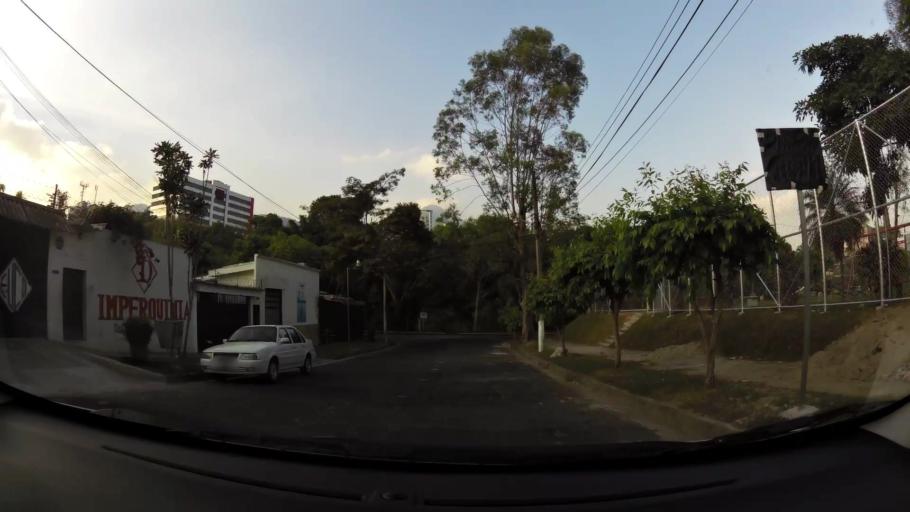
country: SV
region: La Libertad
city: Antiguo Cuscatlan
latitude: 13.7018
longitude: -89.2466
